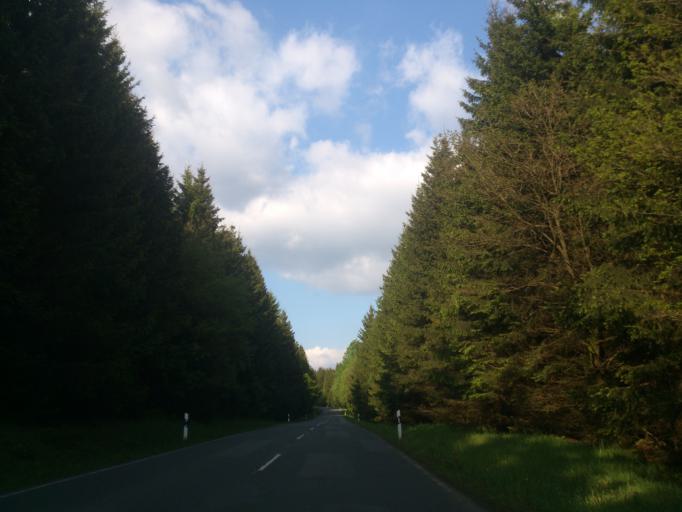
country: DE
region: North Rhine-Westphalia
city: Lichtenau
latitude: 51.6667
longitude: 8.9580
